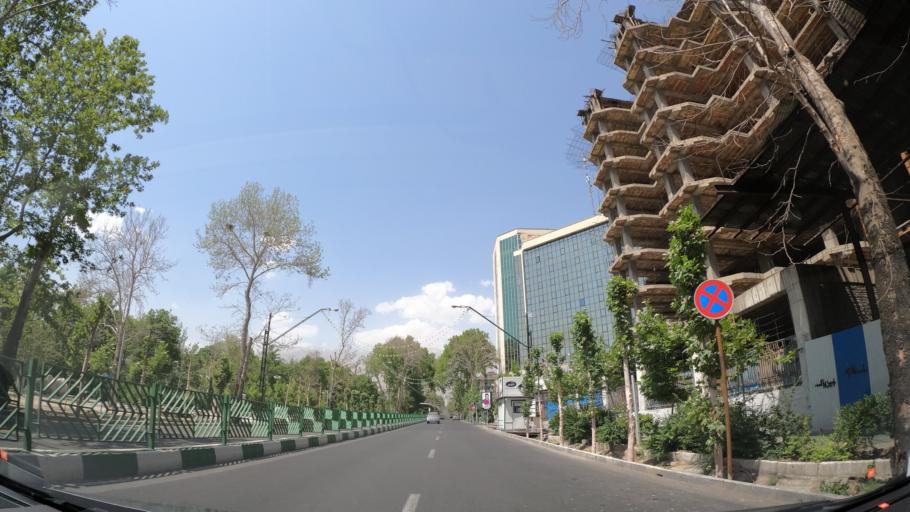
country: IR
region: Tehran
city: Tajrish
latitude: 35.7753
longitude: 51.4129
